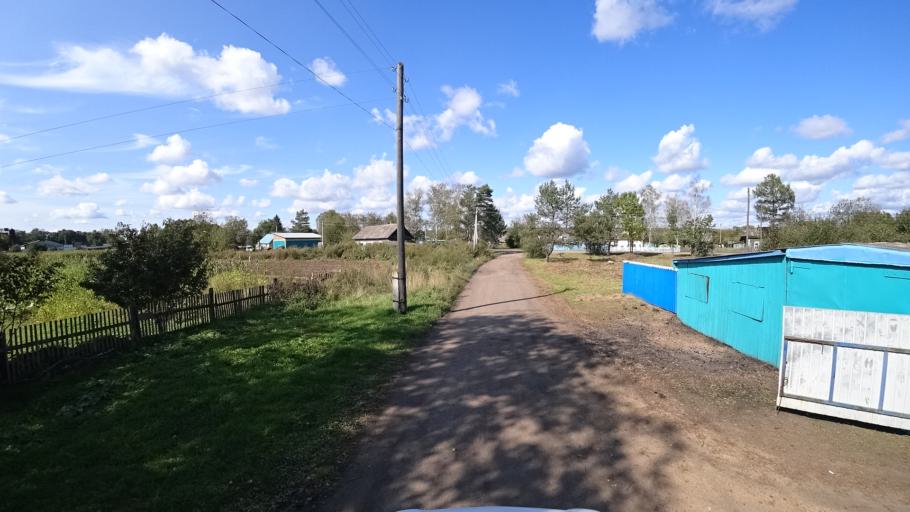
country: RU
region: Amur
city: Arkhara
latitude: 49.4016
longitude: 130.1448
